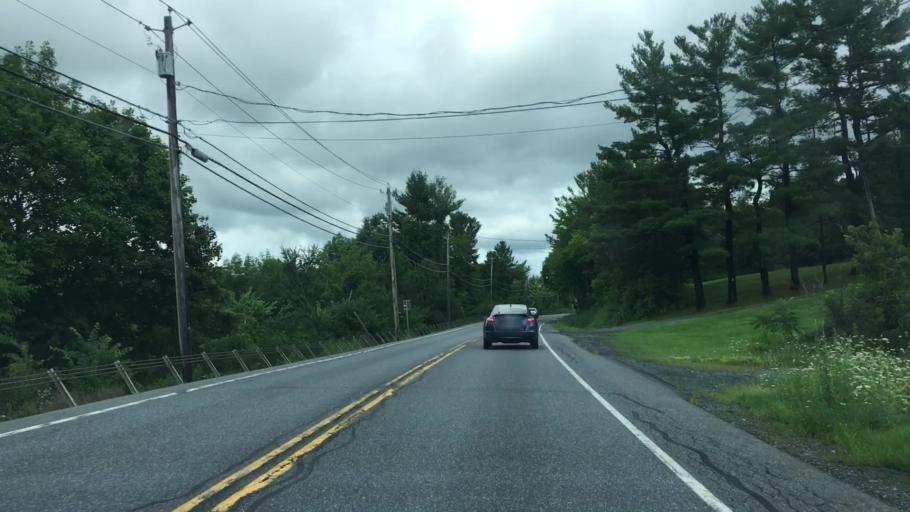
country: US
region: New York
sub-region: Rensselaer County
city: Hoosick Falls
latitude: 42.8390
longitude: -73.4828
